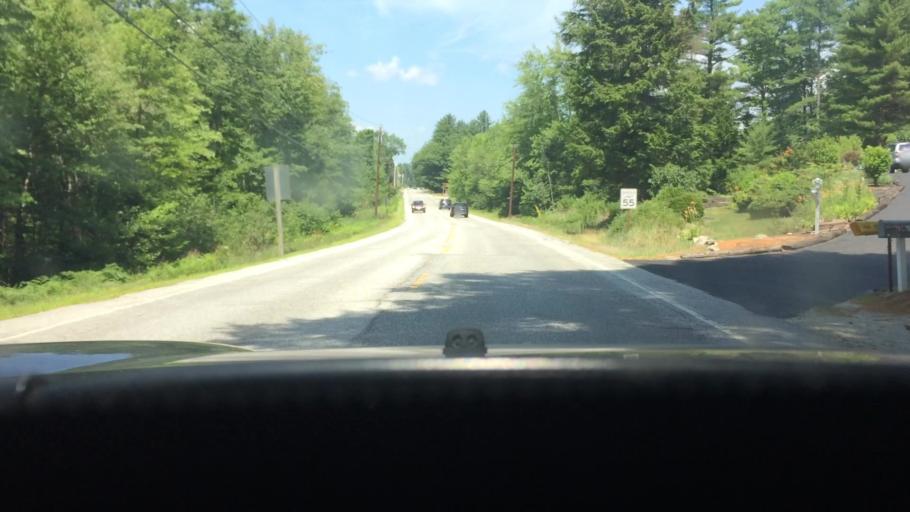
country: US
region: Maine
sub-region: Androscoggin County
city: Mechanic Falls
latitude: 44.1143
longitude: -70.4239
